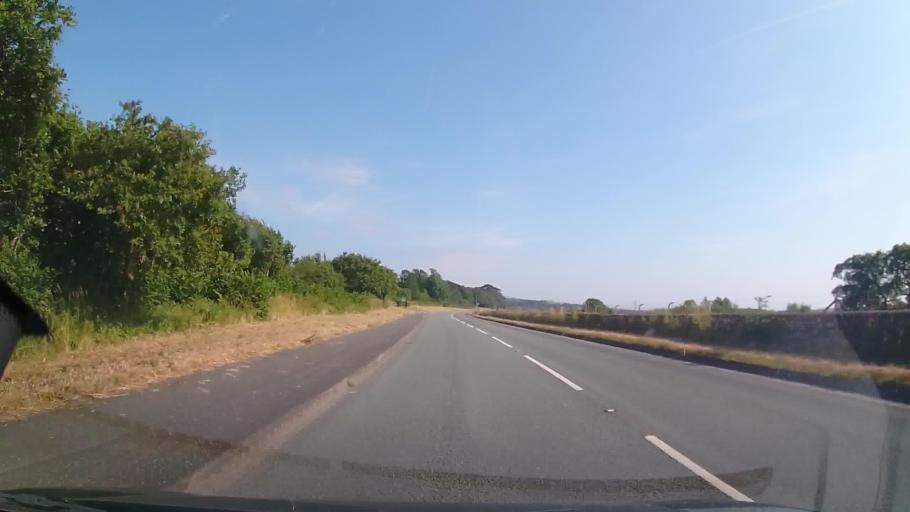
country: GB
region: Wales
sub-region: Gwynedd
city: Llanfair
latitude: 52.8346
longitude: -4.1134
